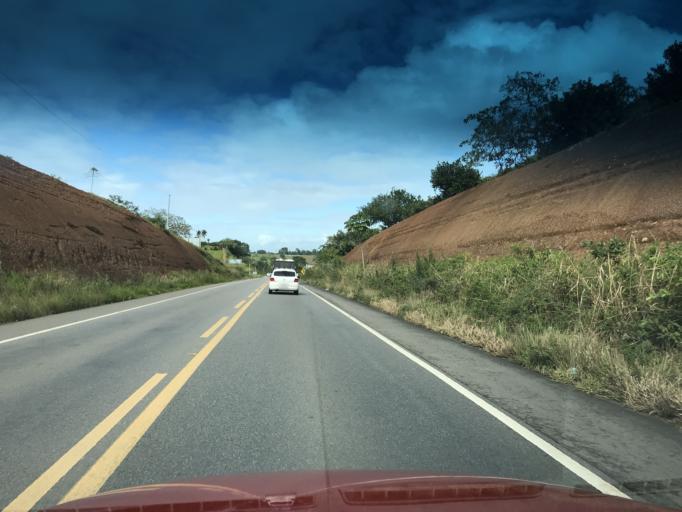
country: BR
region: Bahia
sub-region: Conceicao Do Almeida
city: Muritiba
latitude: -12.9015
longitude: -39.2367
